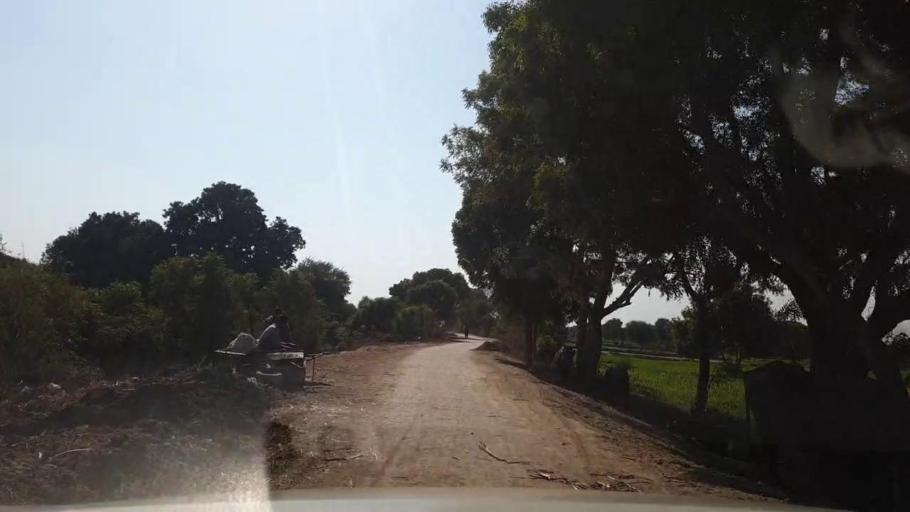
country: PK
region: Sindh
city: Tando Allahyar
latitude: 25.4761
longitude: 68.6950
